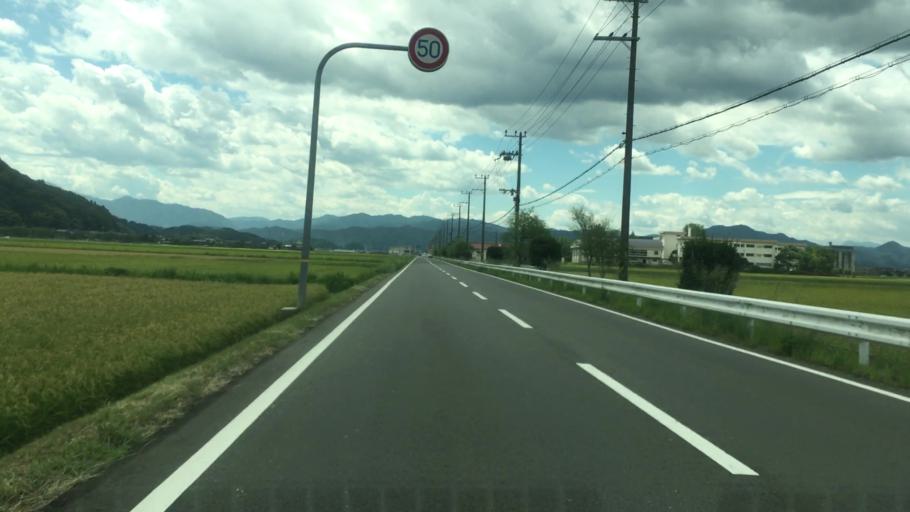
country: JP
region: Hyogo
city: Toyooka
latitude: 35.5339
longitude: 134.8397
